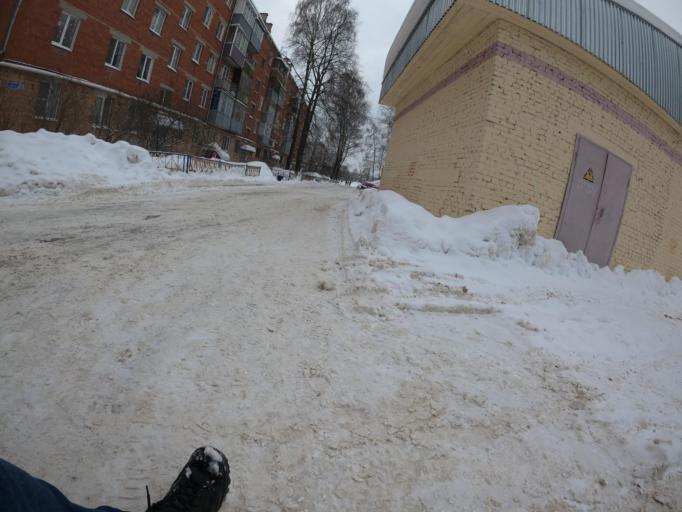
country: RU
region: Moskovskaya
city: Elektrogorsk
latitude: 55.8758
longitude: 38.7865
